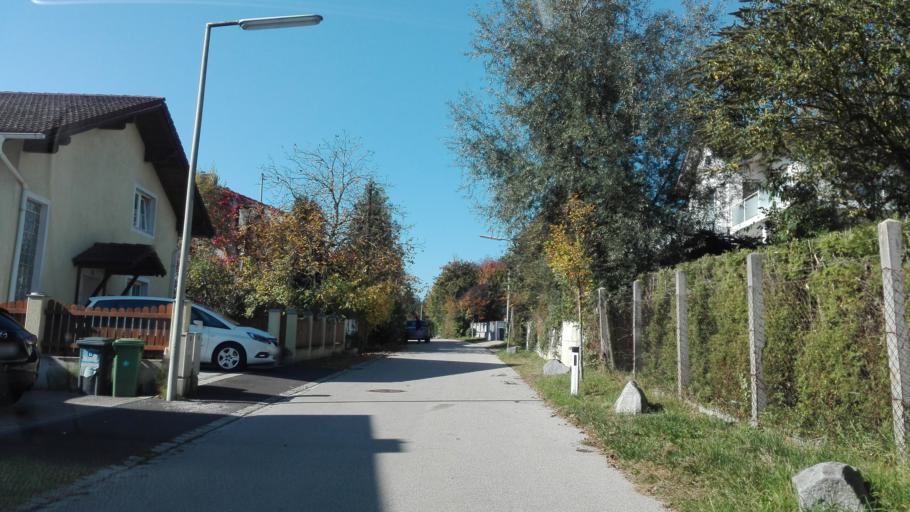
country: AT
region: Upper Austria
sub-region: Politischer Bezirk Linz-Land
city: Leonding
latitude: 48.2847
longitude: 14.2729
